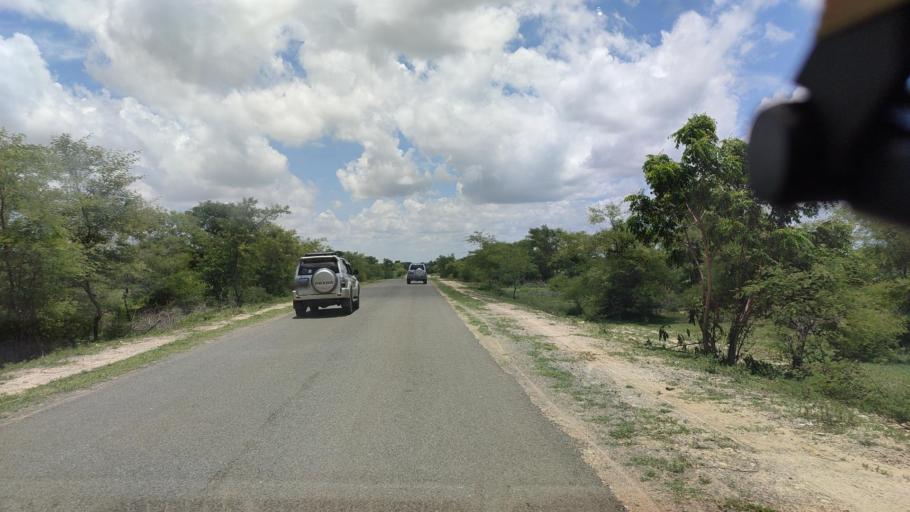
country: MM
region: Magway
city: Taungdwingyi
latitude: 20.1668
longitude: 95.4949
